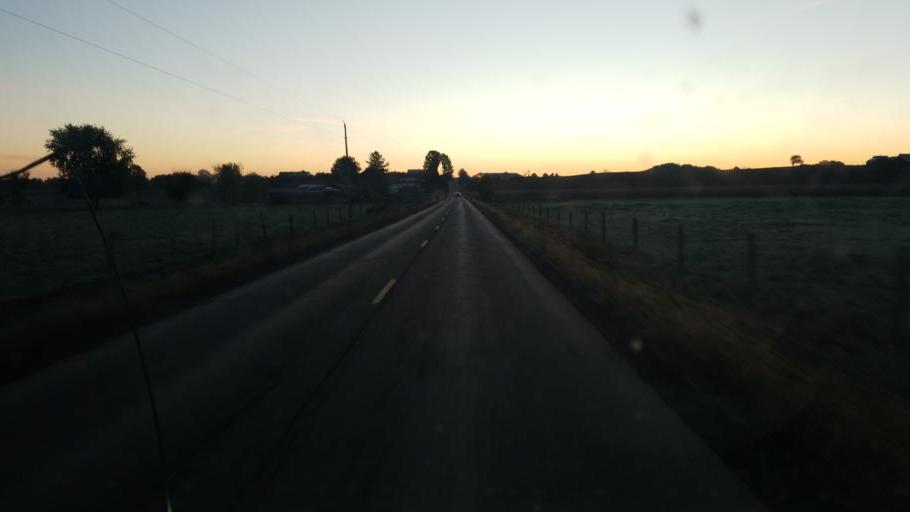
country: US
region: Ohio
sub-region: Wayne County
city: Apple Creek
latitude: 40.7410
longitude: -81.7966
